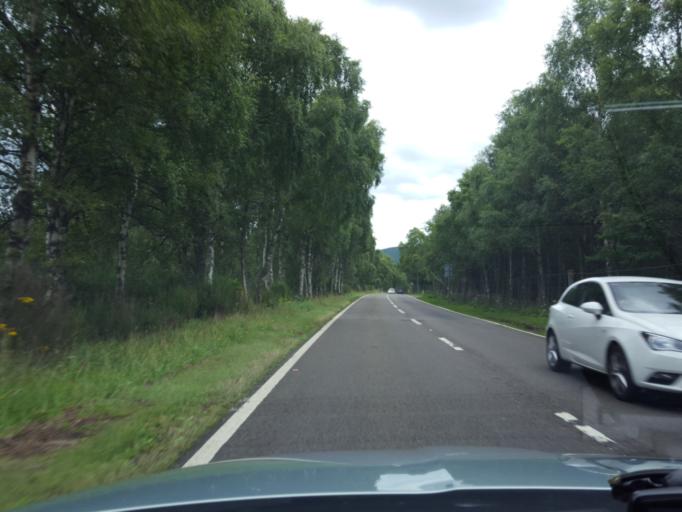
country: GB
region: Scotland
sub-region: Highland
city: Grantown on Spey
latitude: 57.3693
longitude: -3.4997
